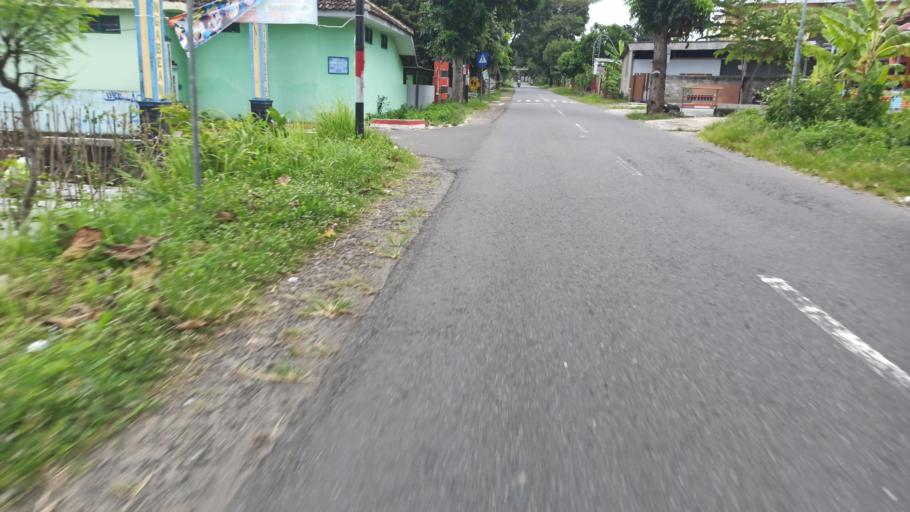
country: ID
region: Daerah Istimewa Yogyakarta
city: Sleman
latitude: -7.6960
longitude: 110.2920
